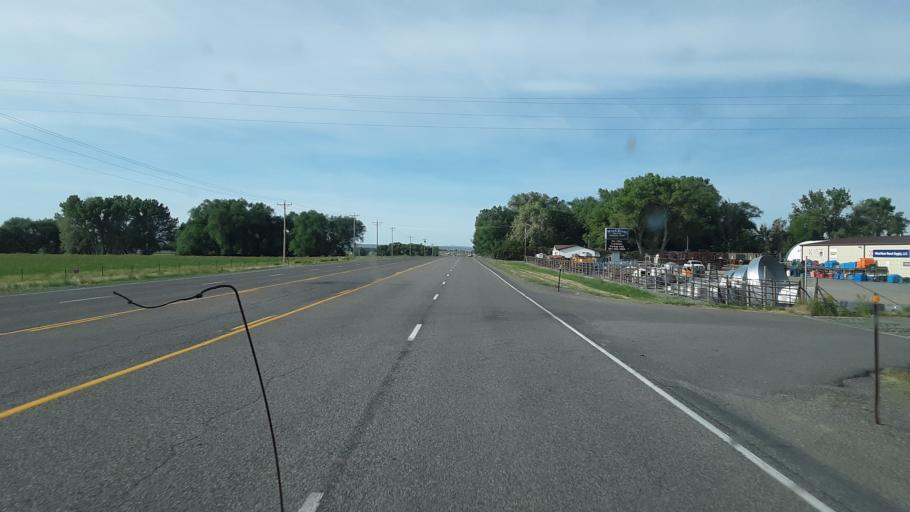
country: US
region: Wyoming
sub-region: Fremont County
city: Riverton
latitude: 43.0670
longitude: -108.3808
